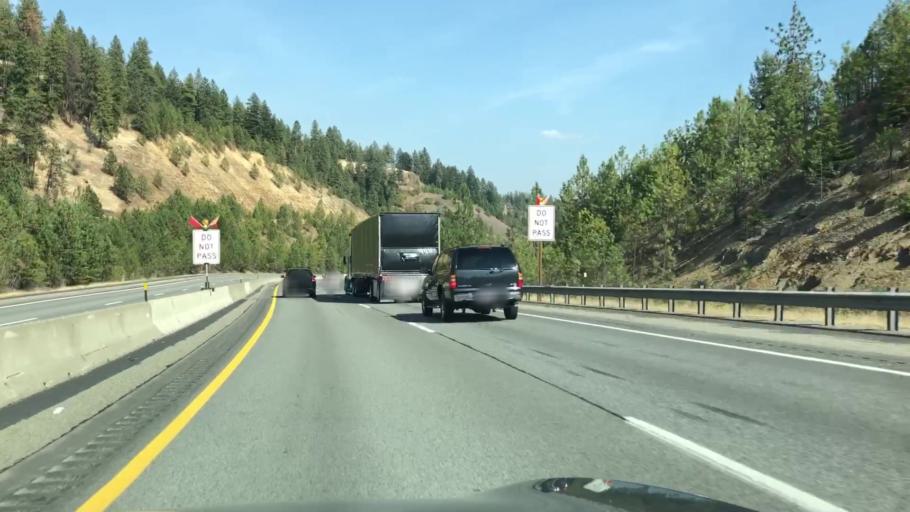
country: US
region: Idaho
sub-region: Kootenai County
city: Coeur d'Alene
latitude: 47.6309
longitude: -116.6970
